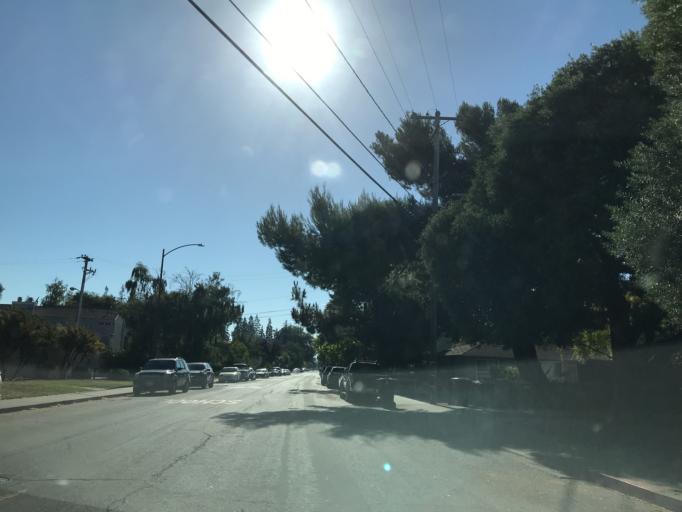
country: US
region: California
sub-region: Santa Clara County
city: Mountain View
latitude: 37.4123
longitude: -122.0868
